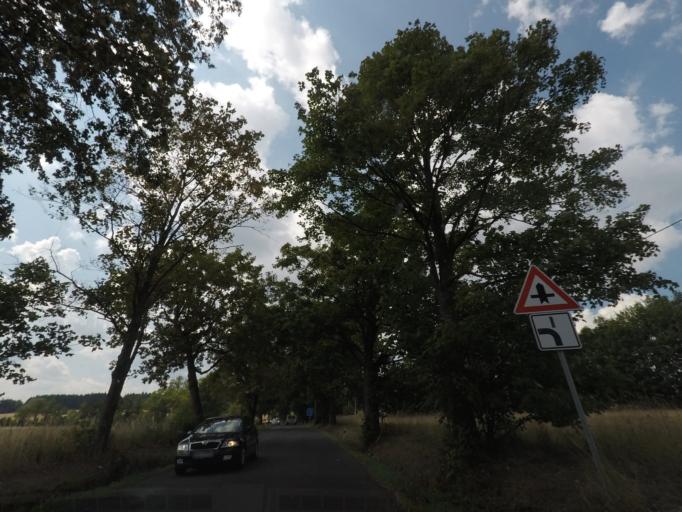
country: CZ
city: Radvanice
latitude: 50.6212
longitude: 16.0706
